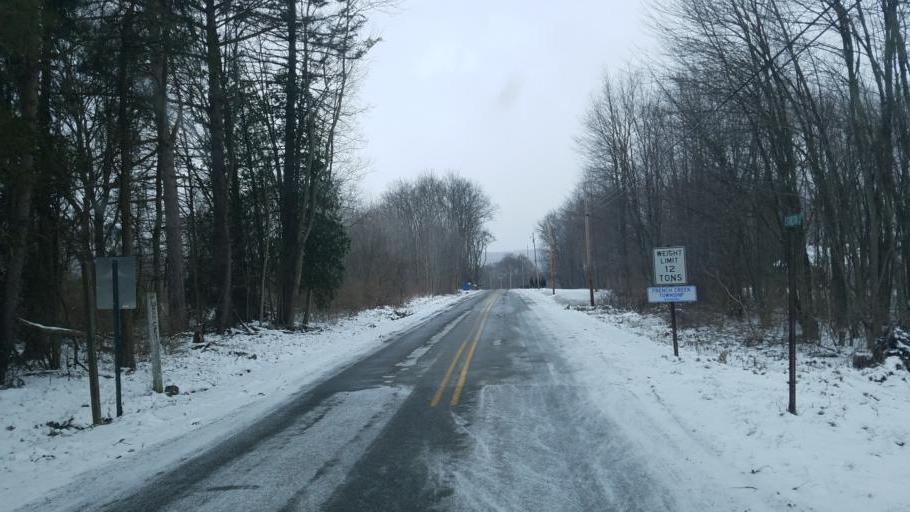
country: US
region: Pennsylvania
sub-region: Crawford County
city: Cochranton
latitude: 41.4762
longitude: -79.9996
